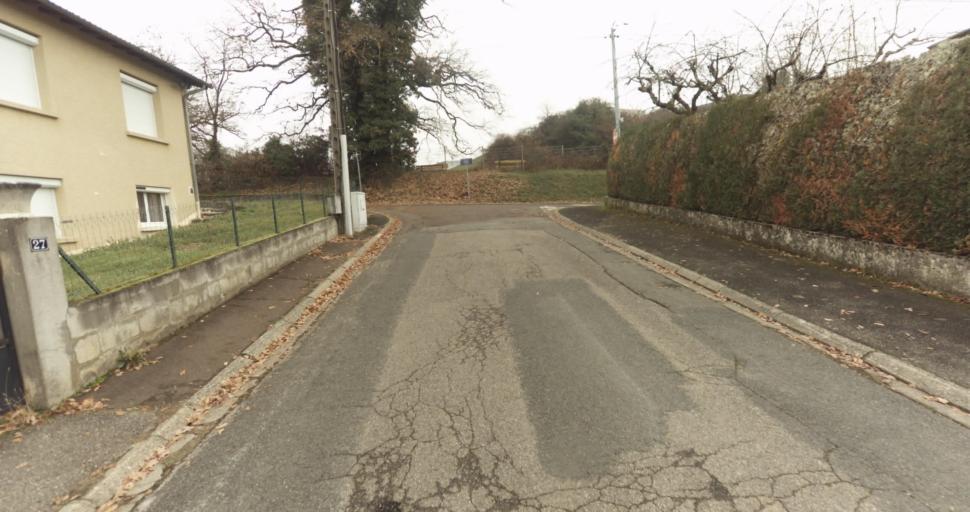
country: FR
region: Midi-Pyrenees
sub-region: Departement du Lot
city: Figeac
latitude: 44.6169
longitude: 2.0344
